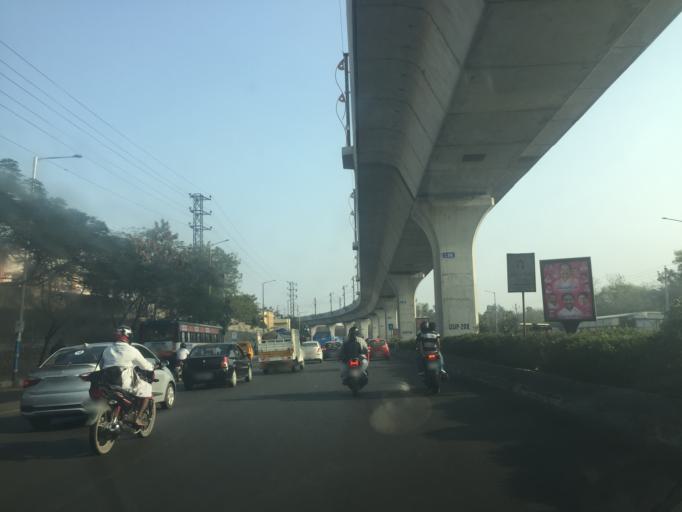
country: IN
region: Telangana
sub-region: Rangareddi
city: Uppal Kalan
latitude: 17.4043
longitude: 78.5571
